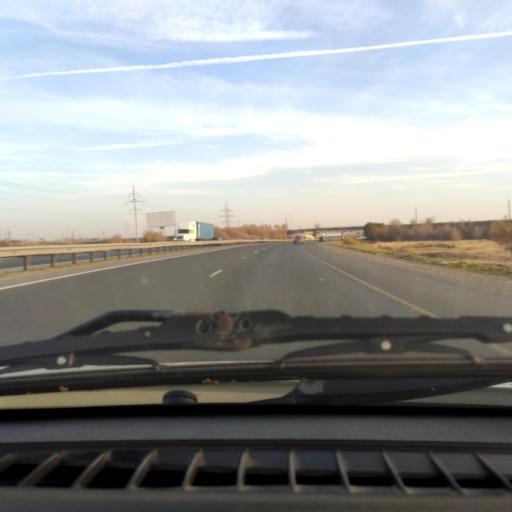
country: RU
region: Samara
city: Tol'yatti
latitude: 53.5654
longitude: 49.4941
